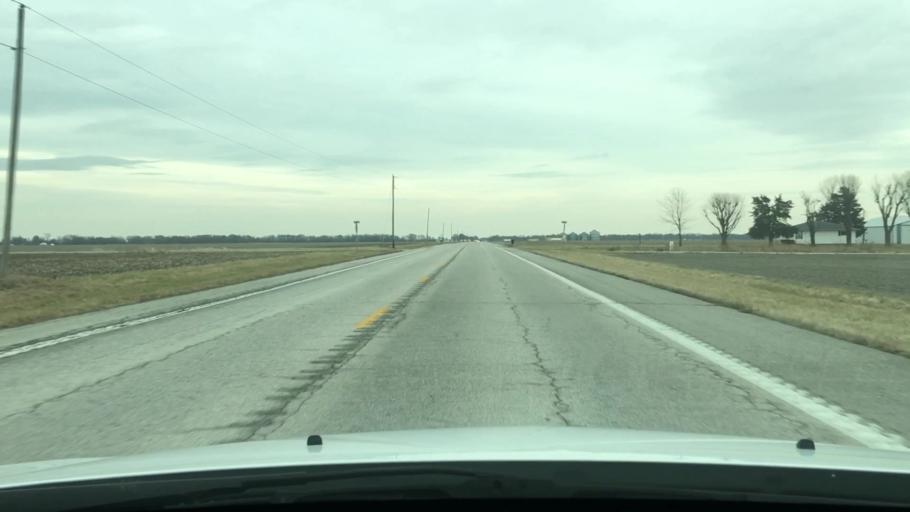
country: US
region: Missouri
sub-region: Audrain County
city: Vandalia
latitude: 39.2801
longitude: -91.6105
